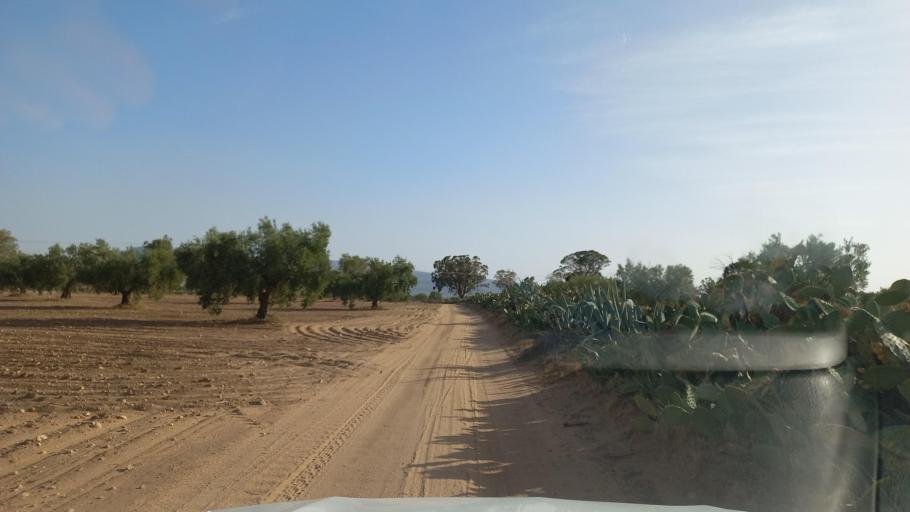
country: TN
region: Al Qasrayn
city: Kasserine
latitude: 35.2251
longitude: 8.9390
